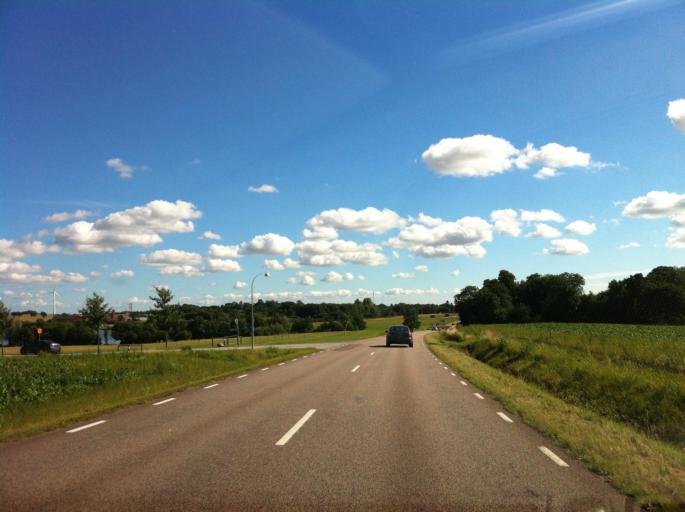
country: SE
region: Skane
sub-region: Svalovs Kommun
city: Kagerod
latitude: 56.0280
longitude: 13.1080
